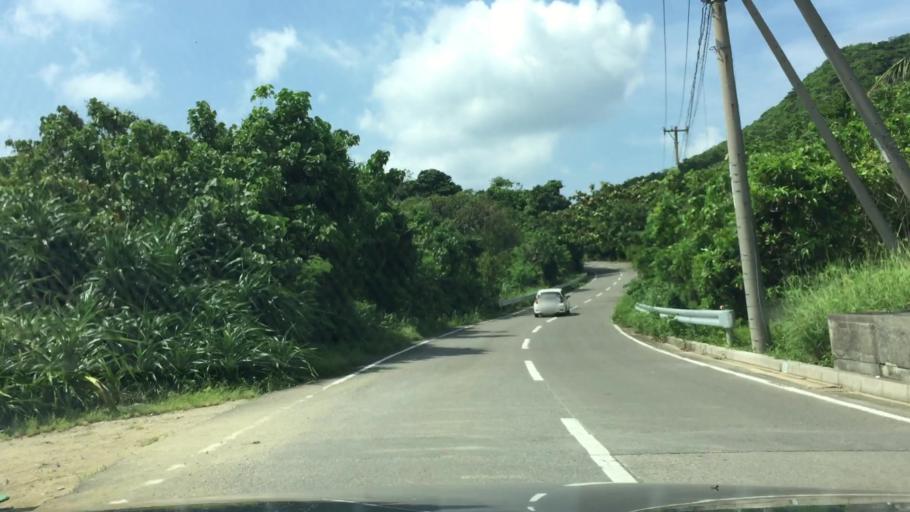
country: JP
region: Okinawa
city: Ishigaki
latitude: 24.4673
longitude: 124.2257
